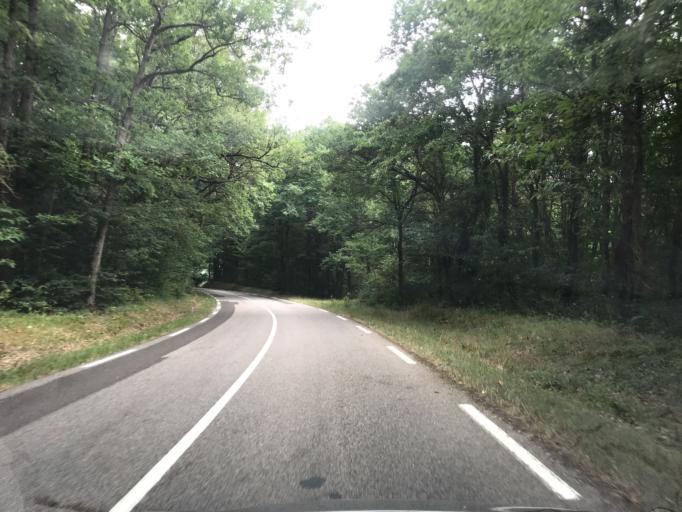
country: FR
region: Haute-Normandie
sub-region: Departement de l'Eure
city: Menilles
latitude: 49.0406
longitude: 1.3042
